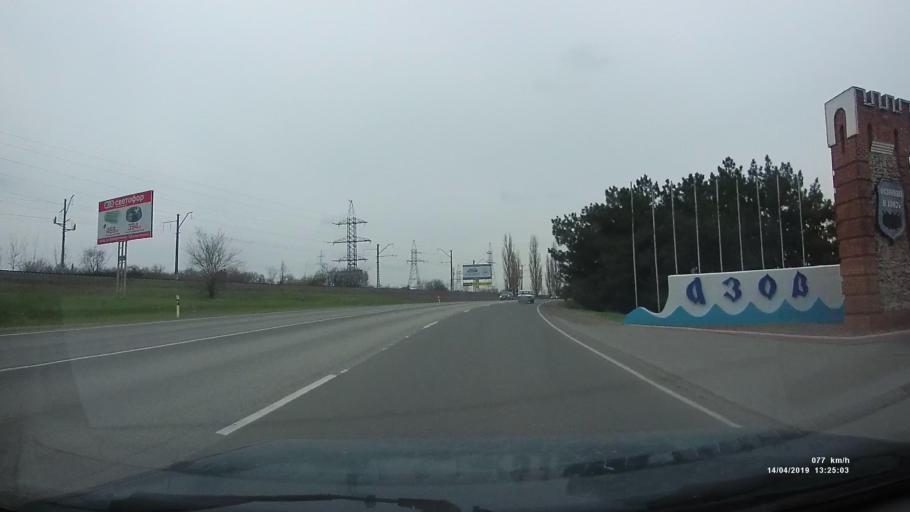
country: RU
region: Rostov
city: Azov
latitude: 47.0844
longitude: 39.4743
